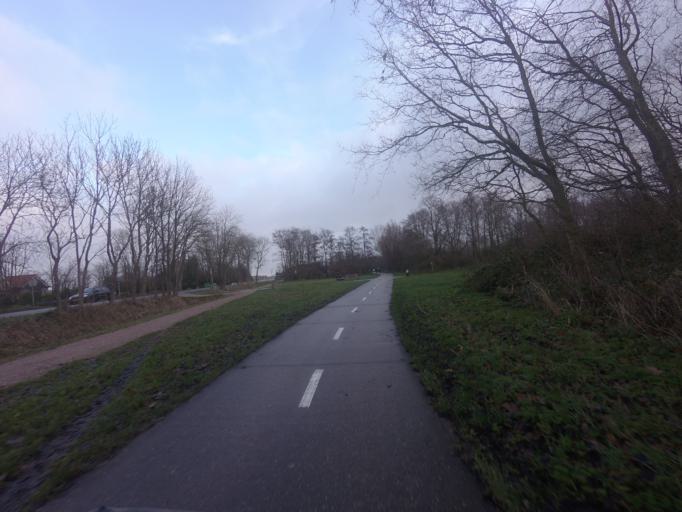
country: NL
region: North Holland
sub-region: Gemeente Texel
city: Den Burg
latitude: 53.1570
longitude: 4.8616
